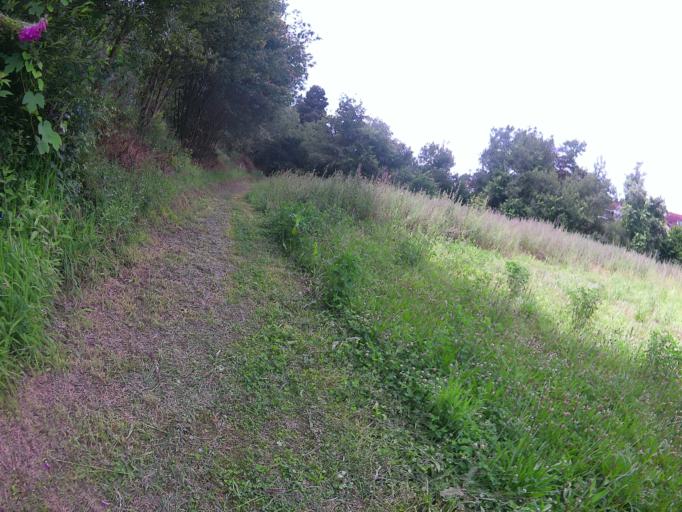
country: PT
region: Aveiro
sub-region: Albergaria-A-Velha
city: Branca
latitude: 40.7645
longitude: -8.4450
